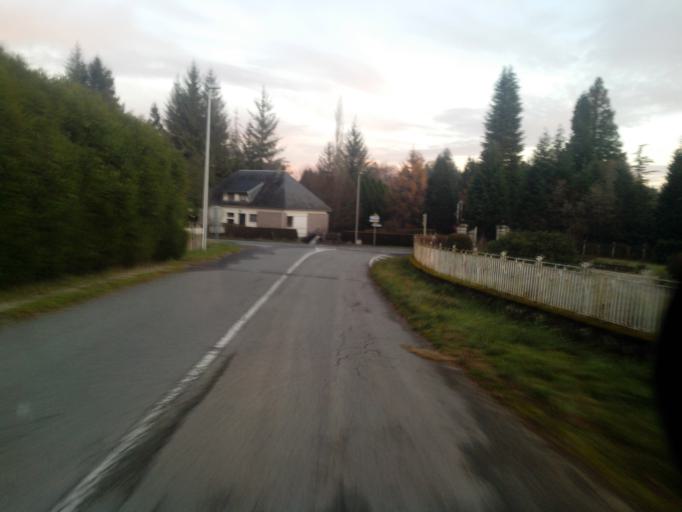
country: FR
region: Limousin
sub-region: Departement de la Correze
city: Meymac
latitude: 45.5446
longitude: 2.1386
